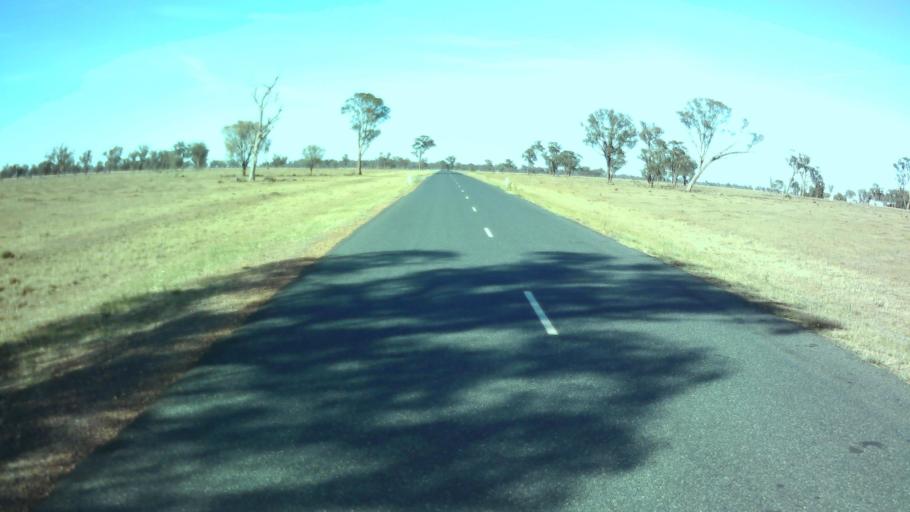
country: AU
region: New South Wales
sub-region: Weddin
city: Grenfell
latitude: -34.0457
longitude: 147.9247
